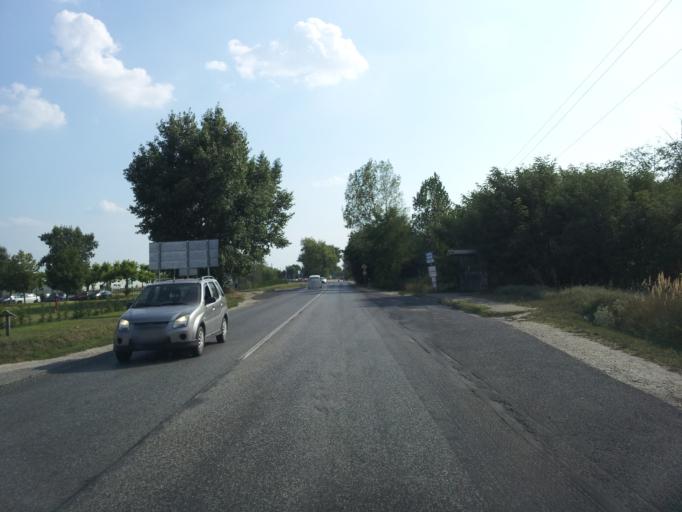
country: HU
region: Pest
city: Szigetszentmiklos
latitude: 47.3099
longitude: 19.0384
